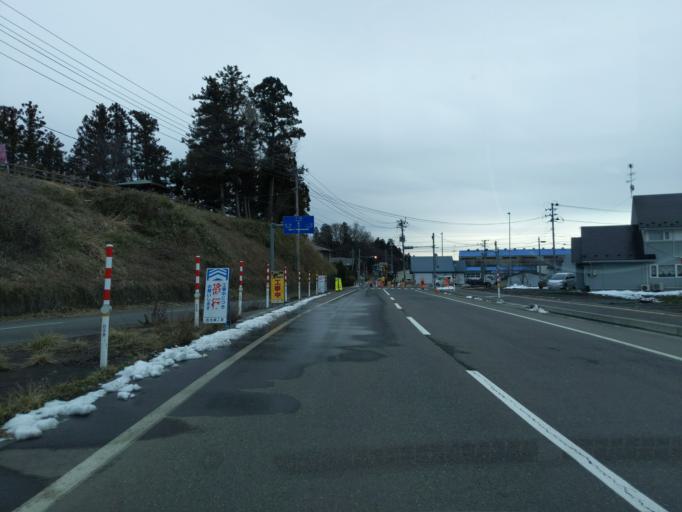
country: JP
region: Iwate
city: Mizusawa
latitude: 39.1800
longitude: 141.1905
